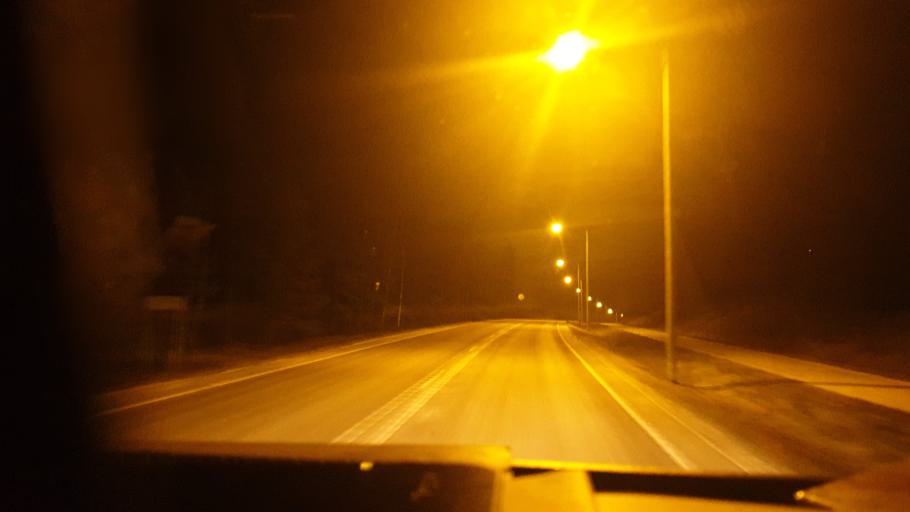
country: FI
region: Southern Ostrobothnia
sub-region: Kuusiokunnat
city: Alavus
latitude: 62.5968
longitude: 23.6495
